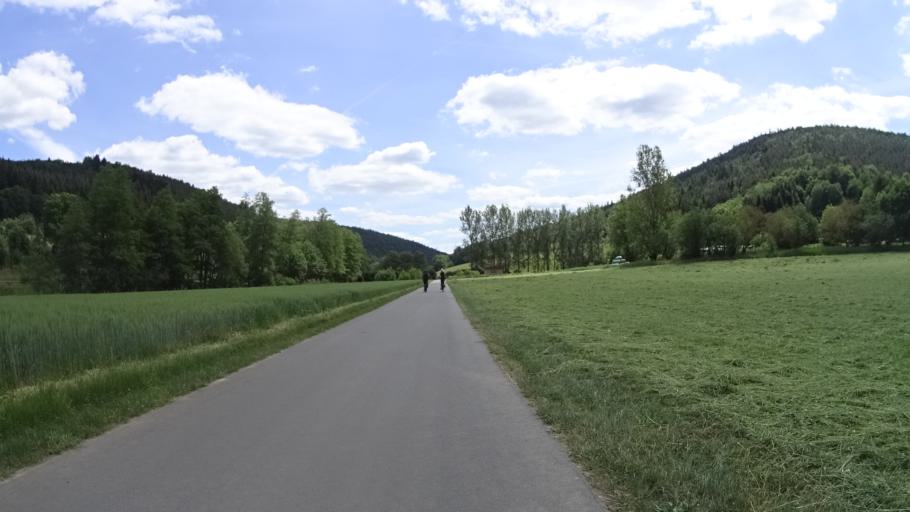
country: DE
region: Bavaria
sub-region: Regierungsbezirk Unterfranken
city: Eichenbuhl
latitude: 49.6929
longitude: 9.3453
